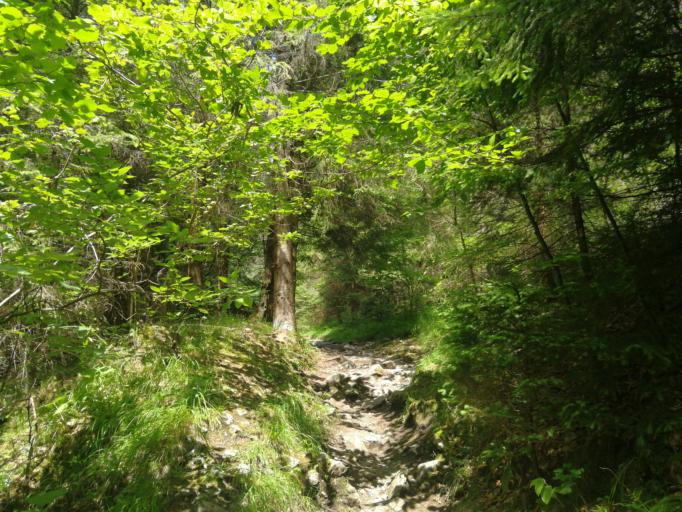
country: SK
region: Zilinsky
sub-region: Okres Liptovsky Mikulas
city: Liptovsky Mikulas
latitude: 49.1639
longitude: 19.4896
